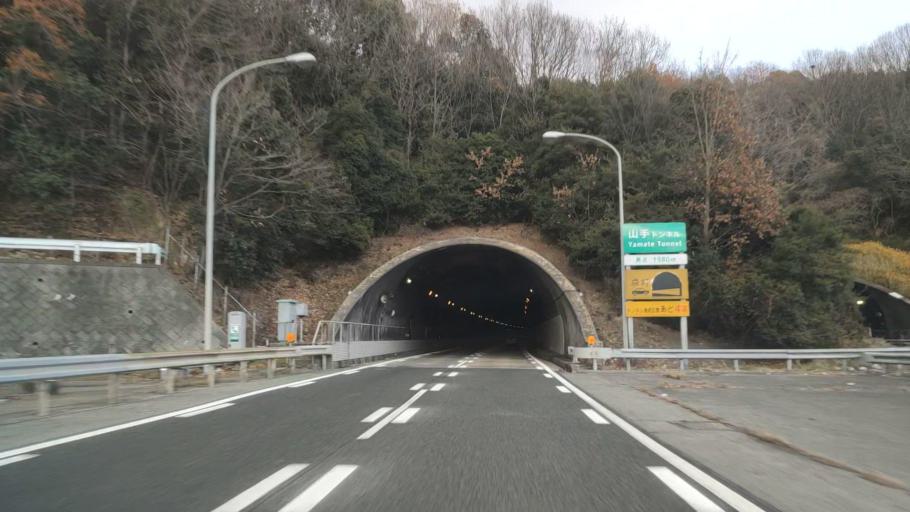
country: JP
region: Hiroshima
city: Fukuyama
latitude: 34.4961
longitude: 133.3178
